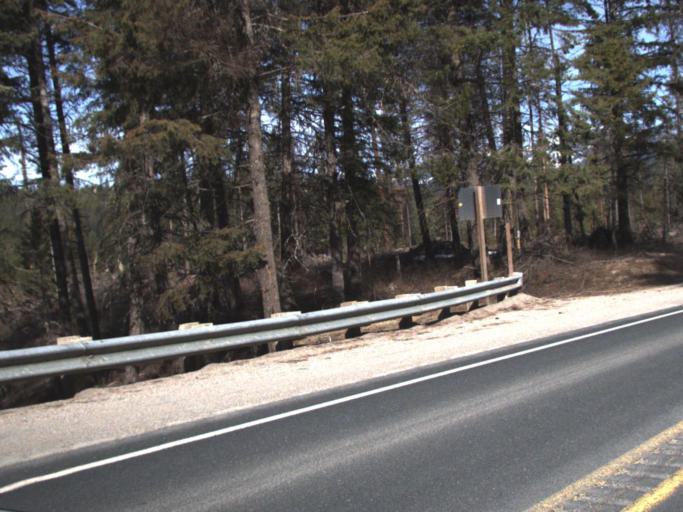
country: US
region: Washington
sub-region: Stevens County
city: Chewelah
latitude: 48.5058
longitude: -117.6731
